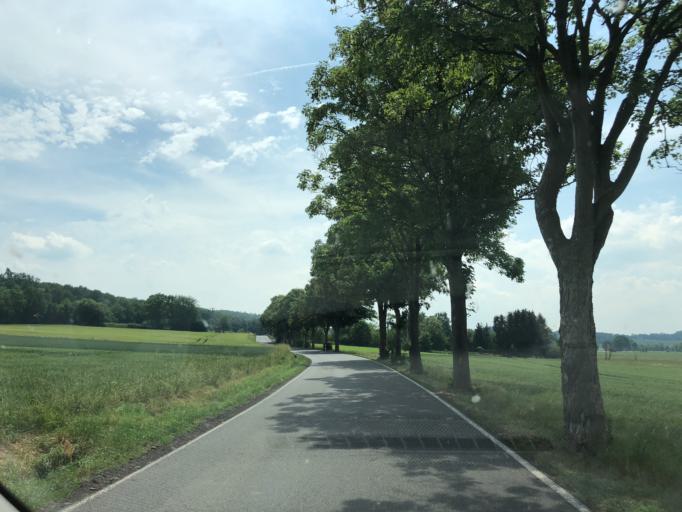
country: DE
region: Hesse
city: Schwalmstadt
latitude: 50.9412
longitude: 9.2016
